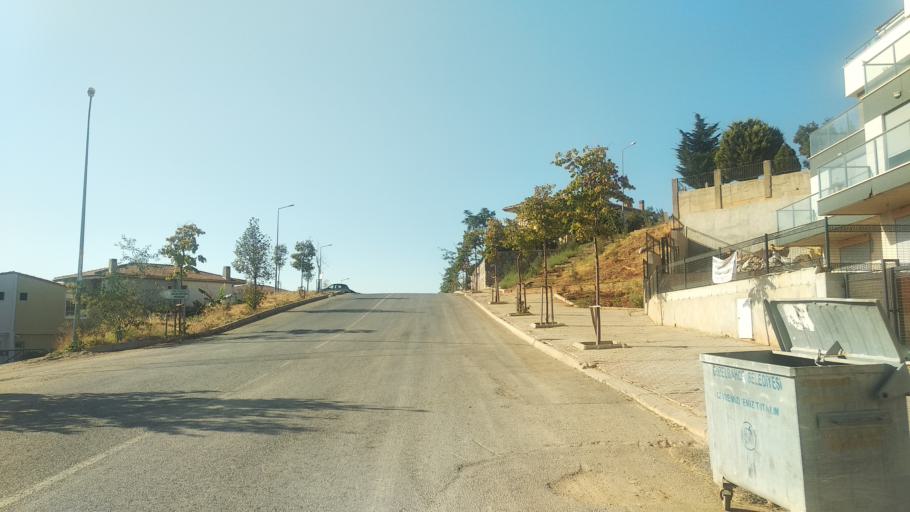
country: TR
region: Izmir
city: Urla
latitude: 38.3588
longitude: 26.8804
